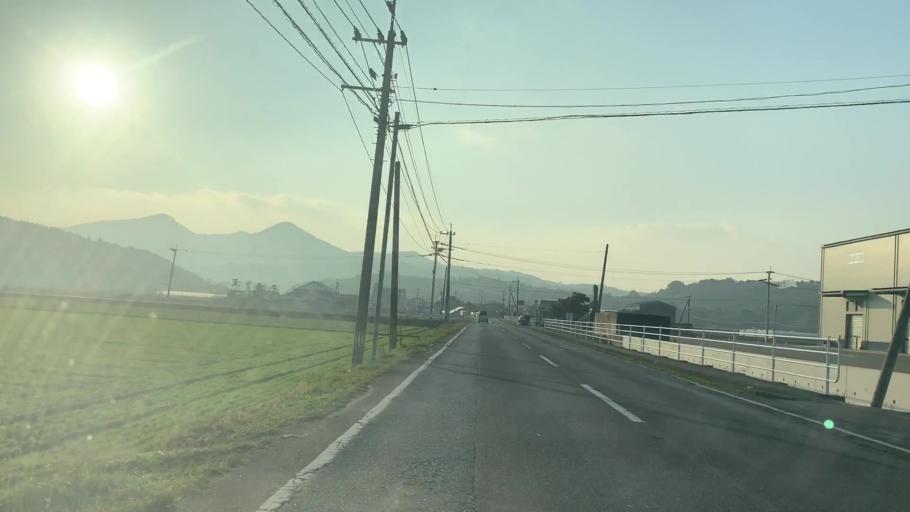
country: JP
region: Saga Prefecture
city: Saga-shi
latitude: 33.2729
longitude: 130.1925
